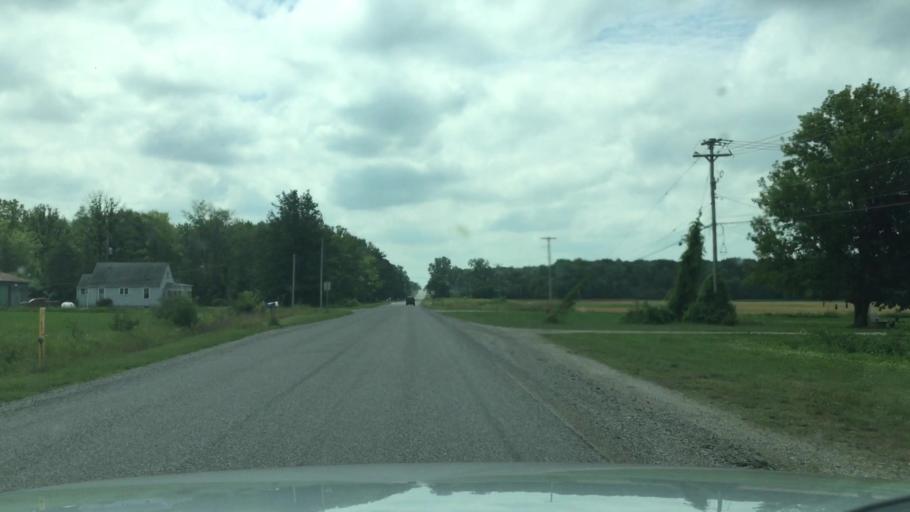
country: US
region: Michigan
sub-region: Saginaw County
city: Birch Run
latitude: 43.2799
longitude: -83.7945
